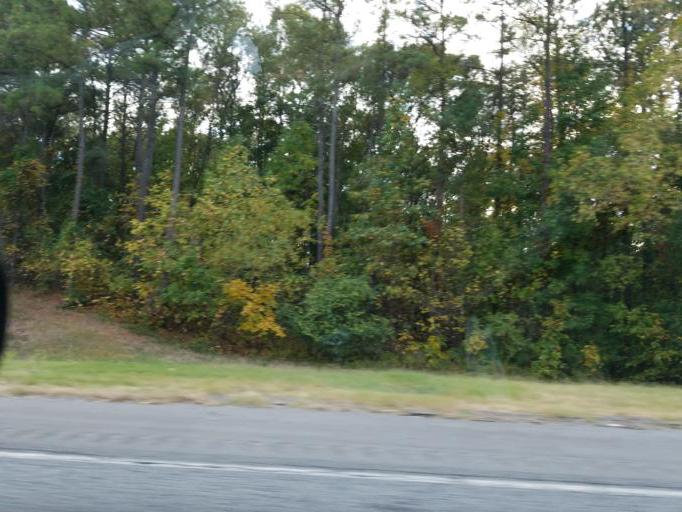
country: US
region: Georgia
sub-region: Bartow County
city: Emerson
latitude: 34.1575
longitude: -84.7520
